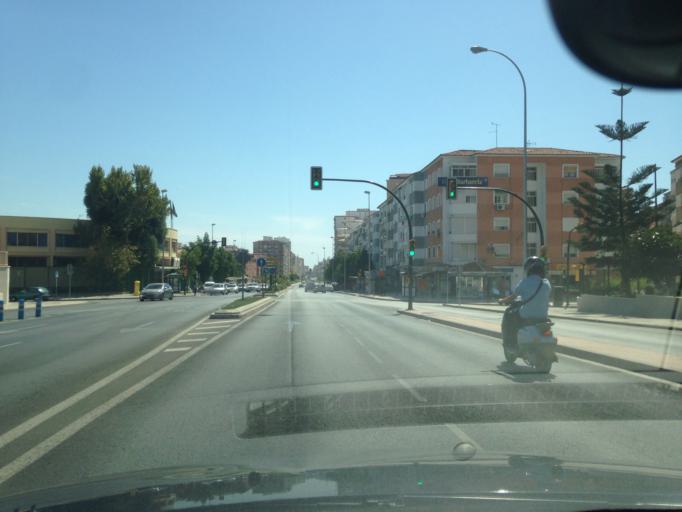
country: ES
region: Andalusia
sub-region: Provincia de Malaga
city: Malaga
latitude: 36.7131
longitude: -4.4472
